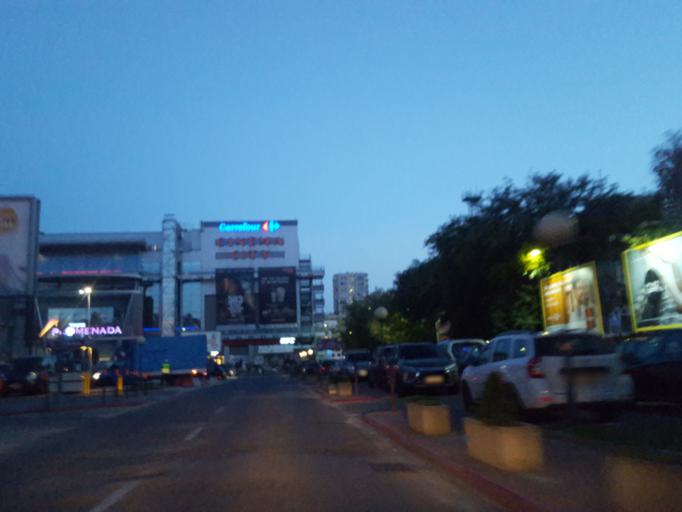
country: PL
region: Masovian Voivodeship
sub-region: Warszawa
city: Praga Poludnie
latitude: 52.2332
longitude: 21.1051
